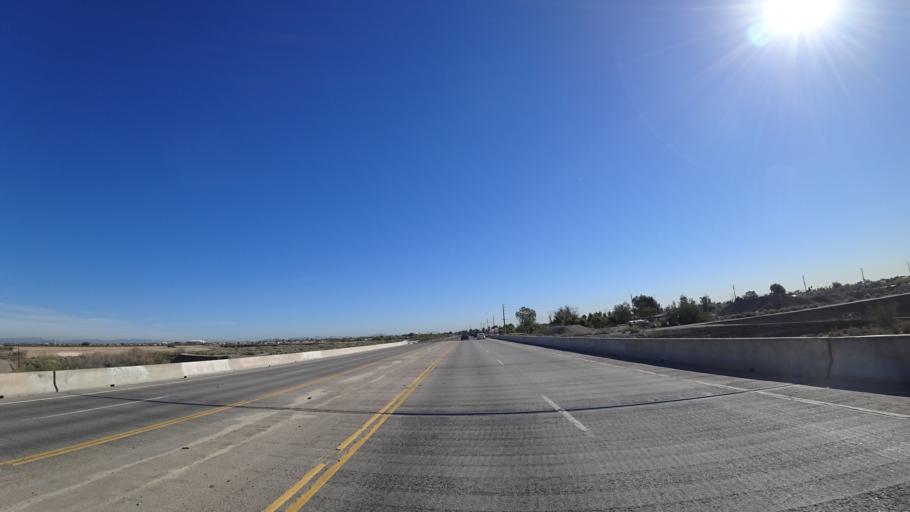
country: US
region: Arizona
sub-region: Maricopa County
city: Litchfield Park
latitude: 33.4931
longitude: -112.3137
